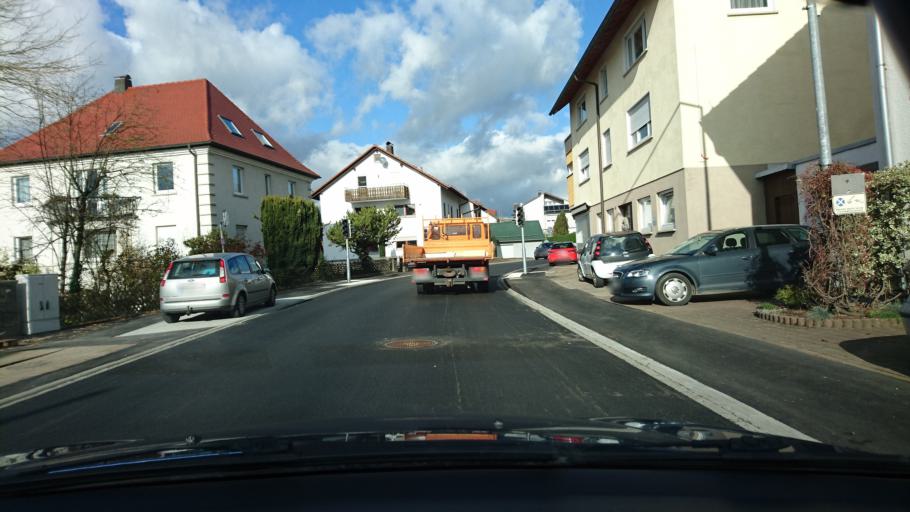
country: DE
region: Baden-Wuerttemberg
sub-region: Regierungsbezirk Stuttgart
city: Huttlingen
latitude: 48.8895
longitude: 10.1005
